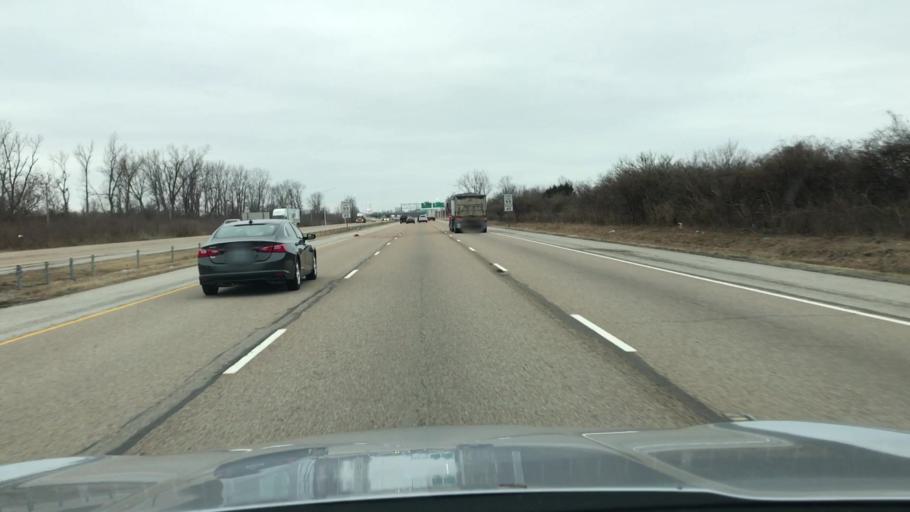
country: US
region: Illinois
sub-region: Saint Clair County
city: Fairmont City
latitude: 38.6507
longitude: -90.1207
